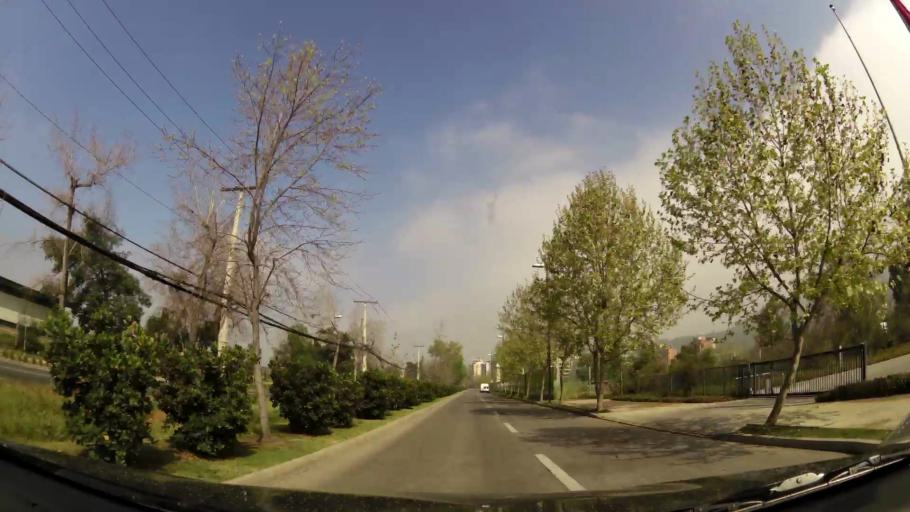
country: CL
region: Santiago Metropolitan
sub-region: Provincia de Santiago
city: Villa Presidente Frei, Nunoa, Santiago, Chile
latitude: -33.3803
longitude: -70.5852
